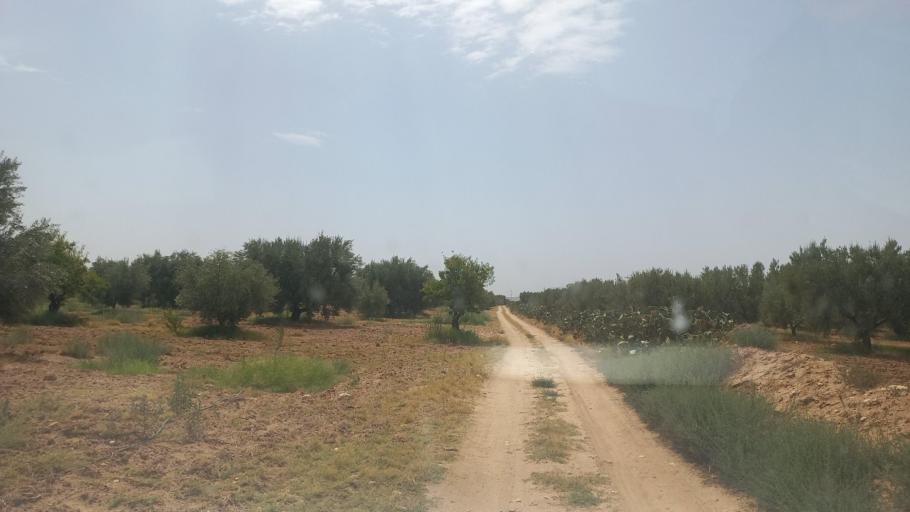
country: TN
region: Al Qasrayn
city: Kasserine
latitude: 35.2647
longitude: 9.0007
